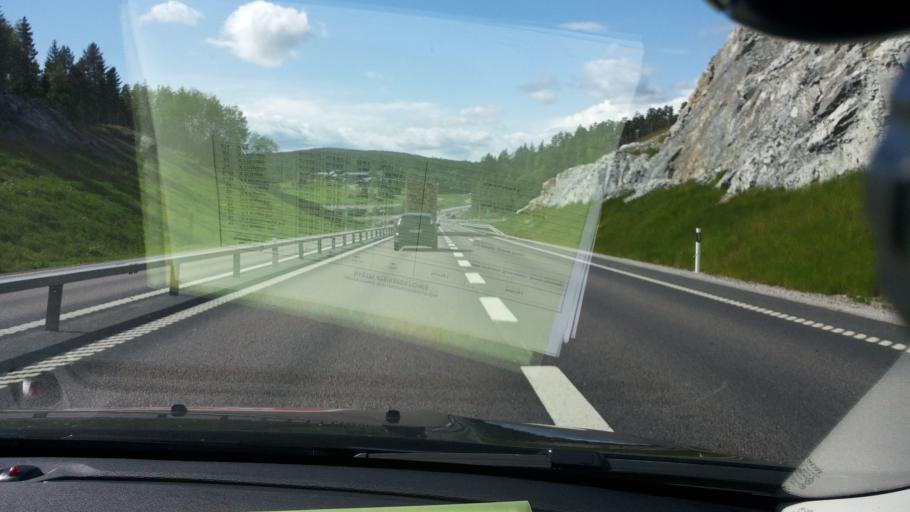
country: SE
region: Vaesternorrland
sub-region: Sundsvalls Kommun
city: Nolby
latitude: 62.2640
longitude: 17.3566
